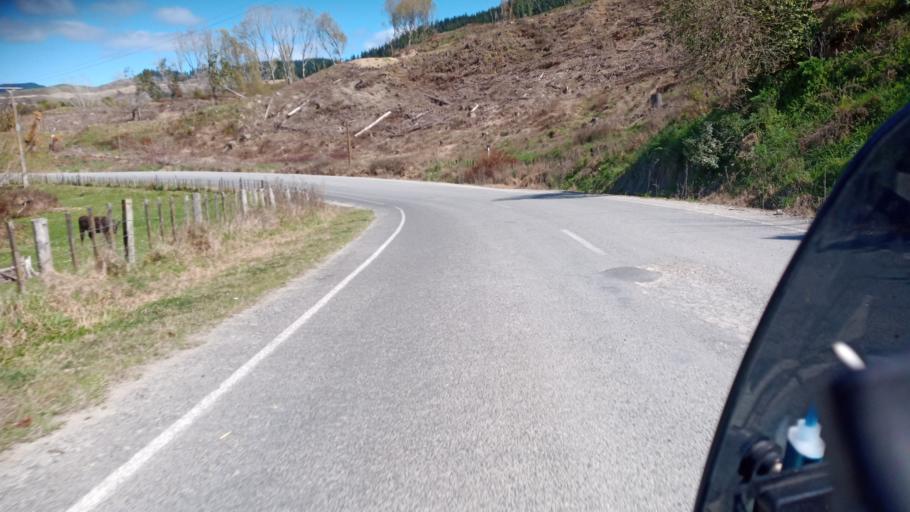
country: NZ
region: Gisborne
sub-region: Gisborne District
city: Gisborne
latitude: -38.7673
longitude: 177.8112
